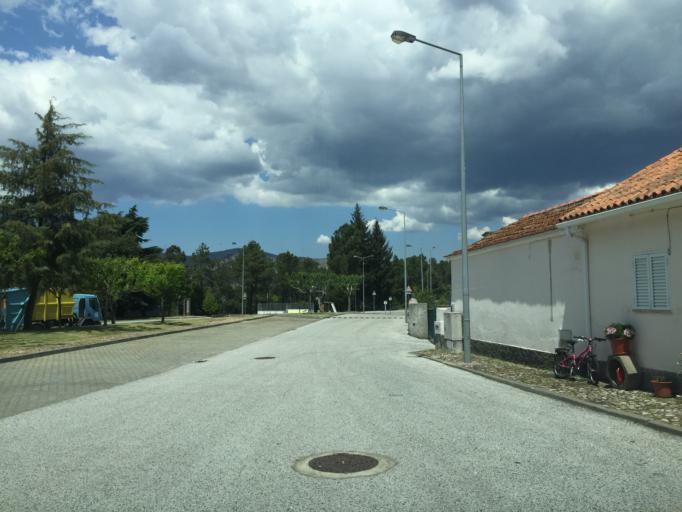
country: PT
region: Coimbra
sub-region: Pampilhosa da Serra
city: Pampilhosa da Serra
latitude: 40.0901
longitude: -7.8499
